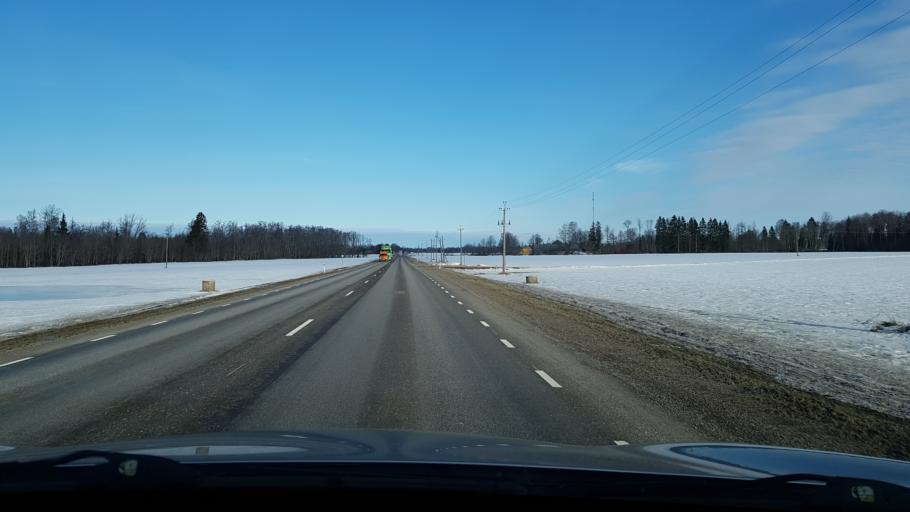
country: EE
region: Viljandimaa
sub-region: Viljandi linn
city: Viljandi
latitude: 58.4503
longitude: 25.5954
